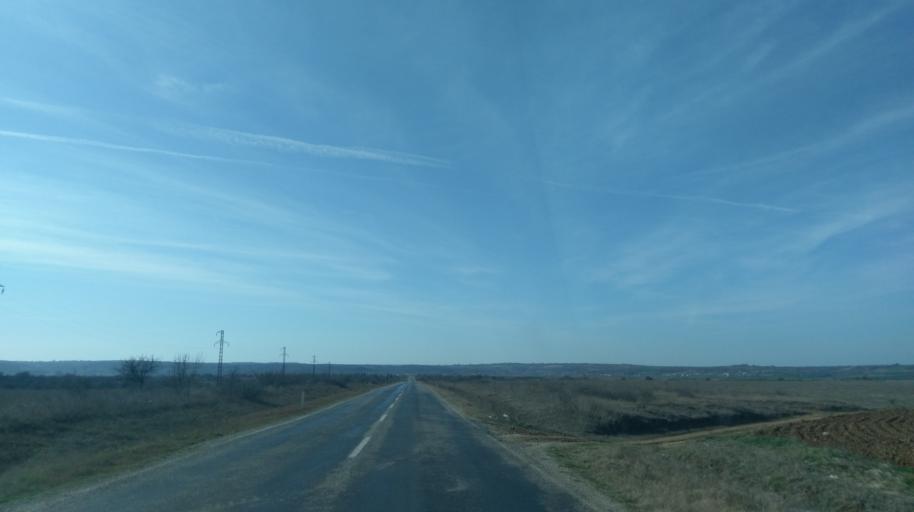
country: TR
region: Edirne
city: Copkoy
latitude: 41.2942
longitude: 26.8130
